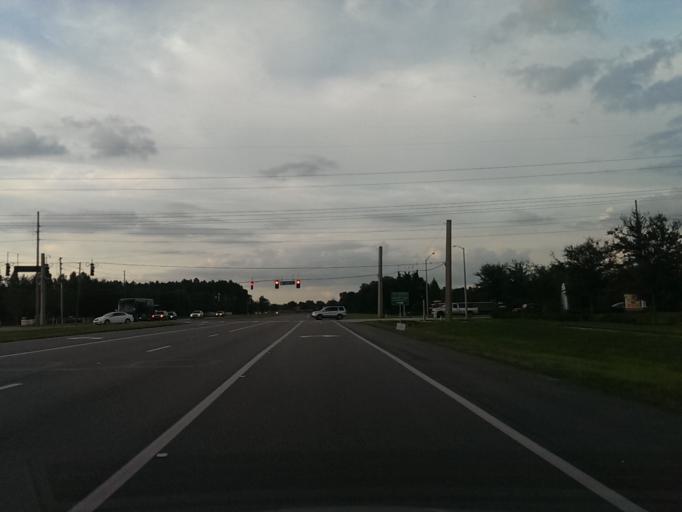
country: US
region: Florida
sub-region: Orange County
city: Windermere
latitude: 28.4635
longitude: -81.5613
